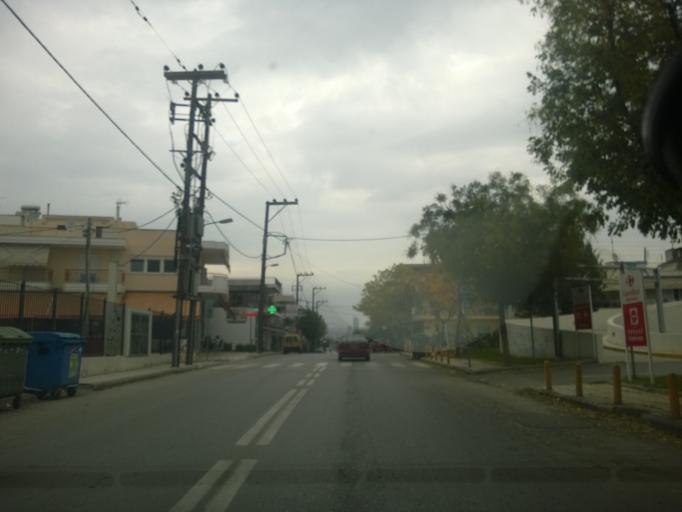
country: GR
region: Central Macedonia
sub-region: Nomos Thessalonikis
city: Stavroupoli
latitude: 40.6752
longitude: 22.9355
